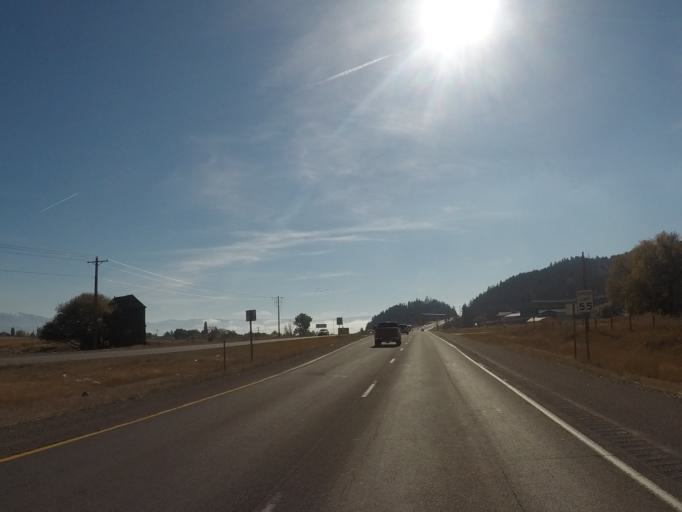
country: US
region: Montana
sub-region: Flathead County
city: Somers
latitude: 48.0989
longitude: -114.2404
